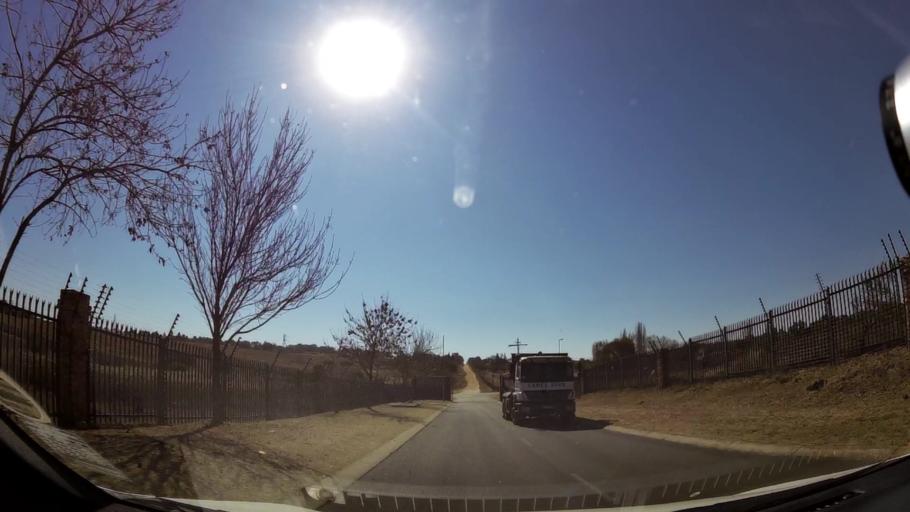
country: ZA
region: Gauteng
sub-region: City of Johannesburg Metropolitan Municipality
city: Midrand
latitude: -25.9494
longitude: 28.0829
